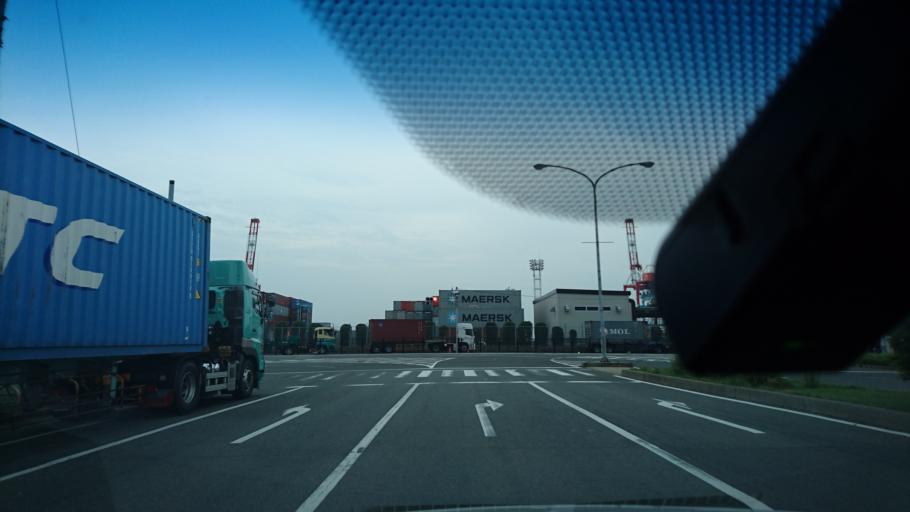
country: JP
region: Hyogo
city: Ashiya
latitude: 34.6826
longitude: 135.2620
